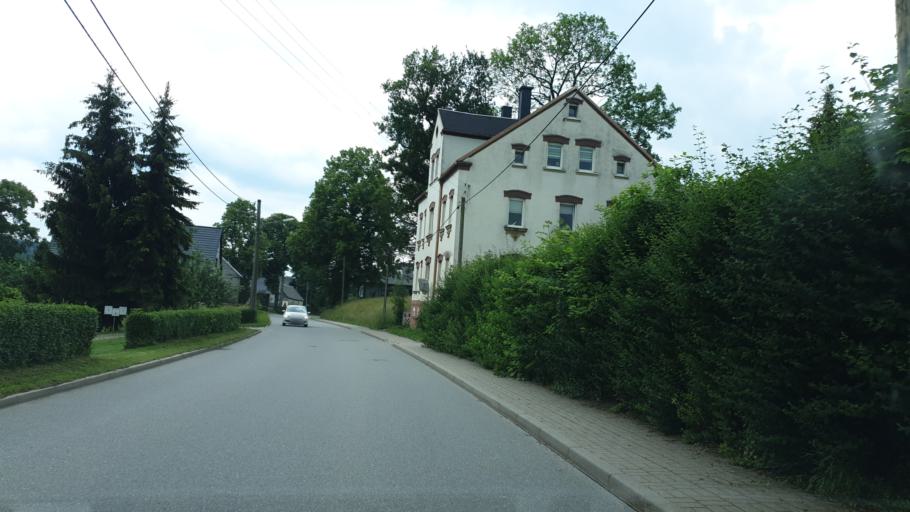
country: DE
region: Saxony
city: Lossnitz
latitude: 50.6199
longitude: 12.7101
